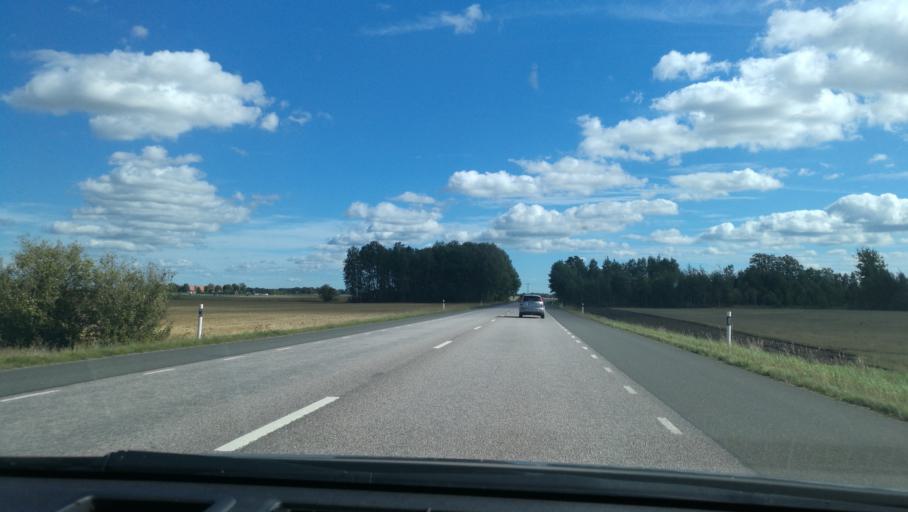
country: SE
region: Vaestra Goetaland
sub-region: Gotene Kommun
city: Kallby
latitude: 58.5111
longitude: 13.3586
